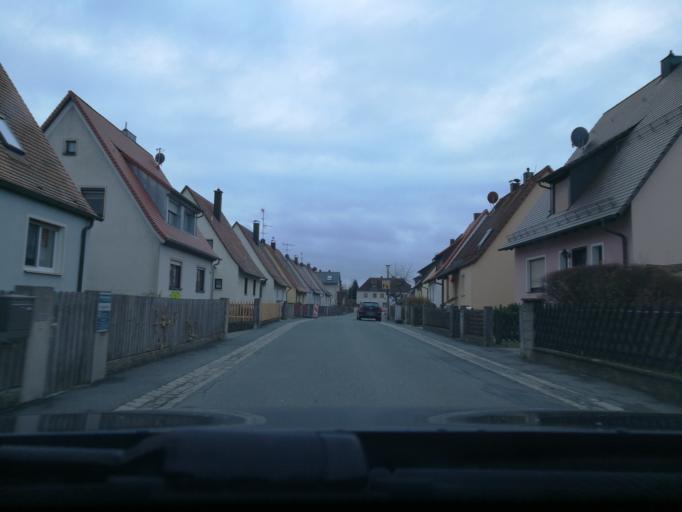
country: DE
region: Bavaria
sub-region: Regierungsbezirk Mittelfranken
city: Kalchreuth
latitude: 49.5588
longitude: 11.1376
